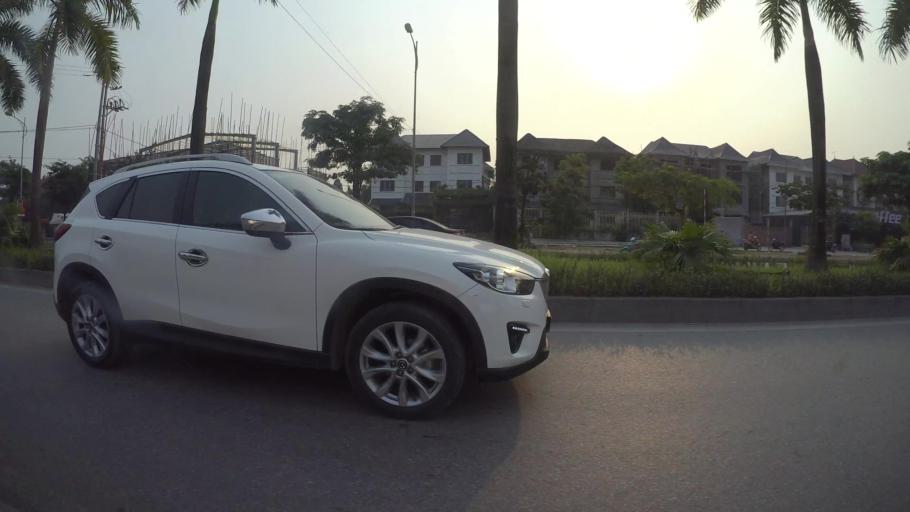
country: VN
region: Ha Noi
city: Cau Dien
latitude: 21.0006
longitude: 105.7336
